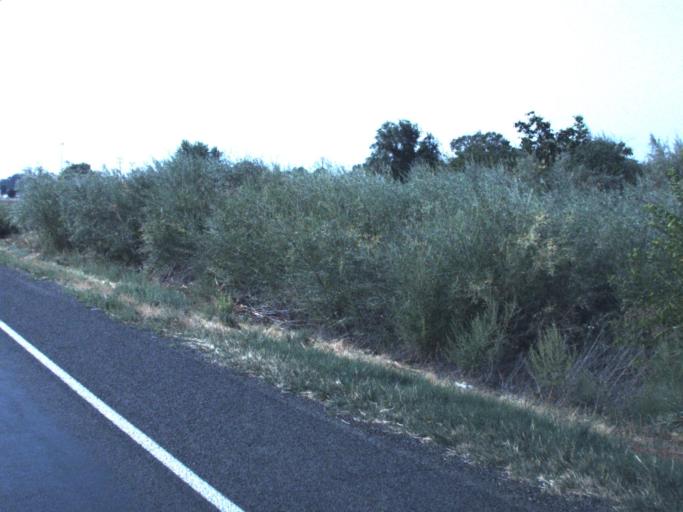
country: US
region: Washington
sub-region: Yakima County
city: Mabton
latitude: 46.2092
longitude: -119.9892
